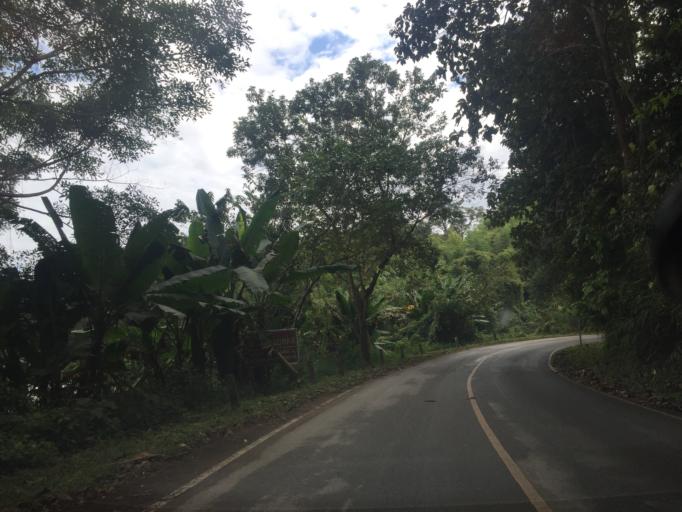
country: TH
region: Lampang
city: Mueang Pan
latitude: 18.8355
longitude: 99.4736
